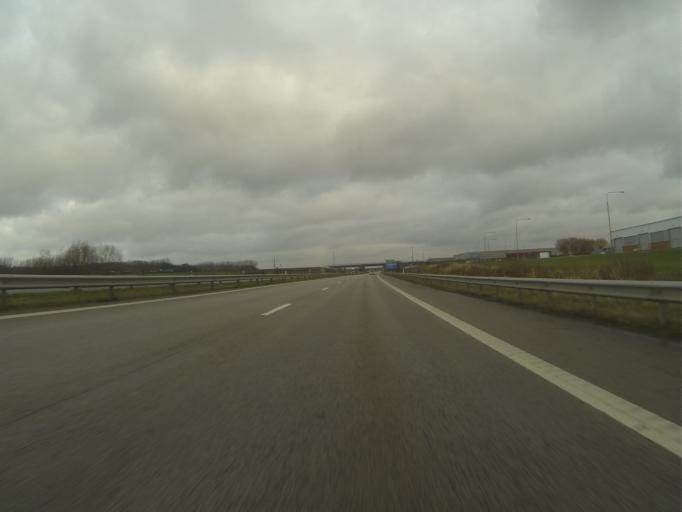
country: SE
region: Skane
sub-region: Burlovs Kommun
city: Arloev
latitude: 55.6453
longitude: 13.0685
